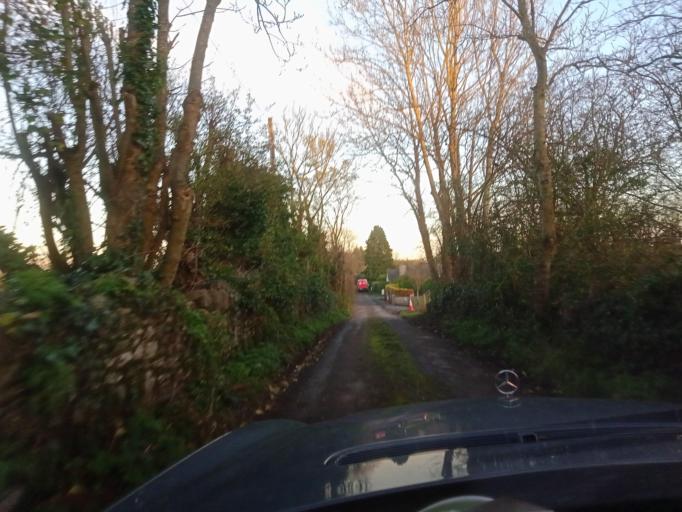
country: IE
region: Leinster
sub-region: Kilkenny
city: Kilkenny
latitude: 52.6105
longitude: -7.1933
